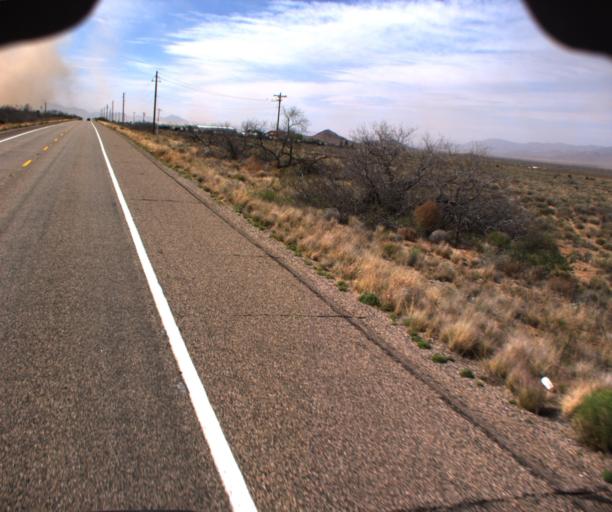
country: US
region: Arizona
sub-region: Mohave County
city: New Kingman-Butler
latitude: 35.4111
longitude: -113.7793
